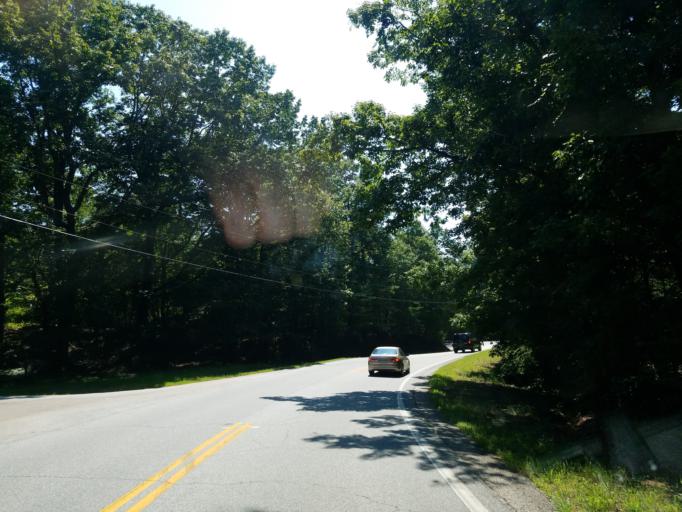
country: US
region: Georgia
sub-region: Lumpkin County
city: Dahlonega
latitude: 34.5908
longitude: -83.9700
